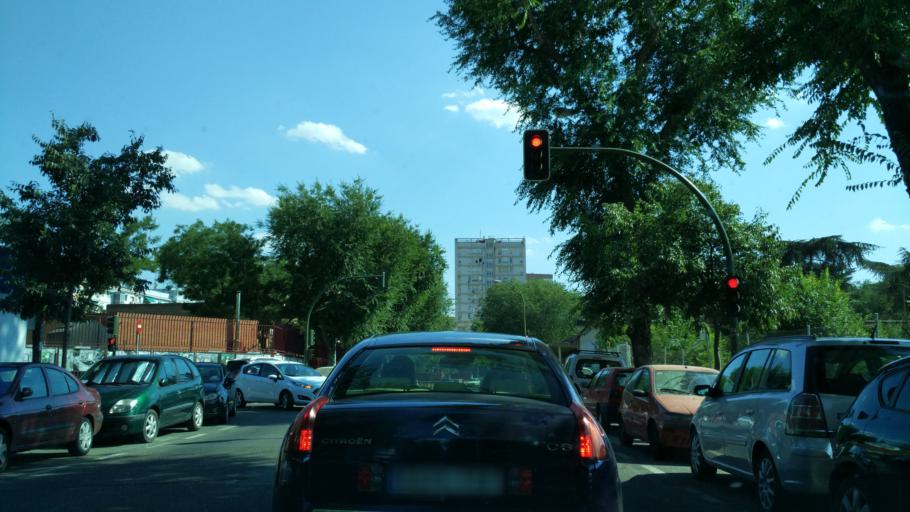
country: ES
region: Madrid
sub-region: Provincia de Madrid
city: Tetuan de las Victorias
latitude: 40.4605
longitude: -3.7123
